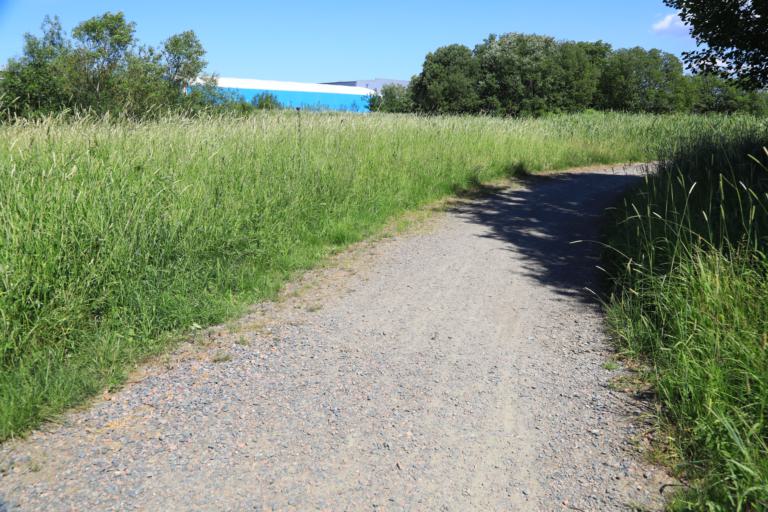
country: SE
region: Halland
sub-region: Kungsbacka Kommun
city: Kungsbacka
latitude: 57.5089
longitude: 12.0765
